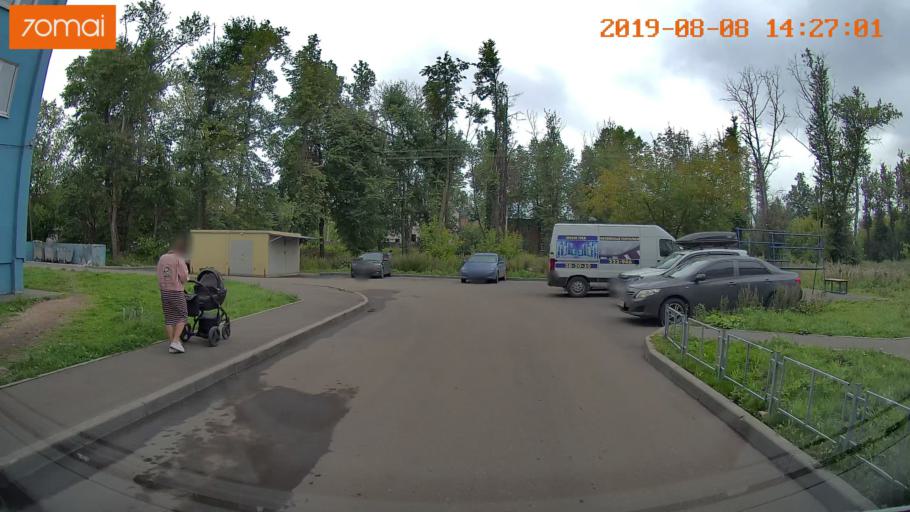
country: RU
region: Ivanovo
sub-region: Gorod Ivanovo
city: Ivanovo
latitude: 56.9987
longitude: 40.9408
